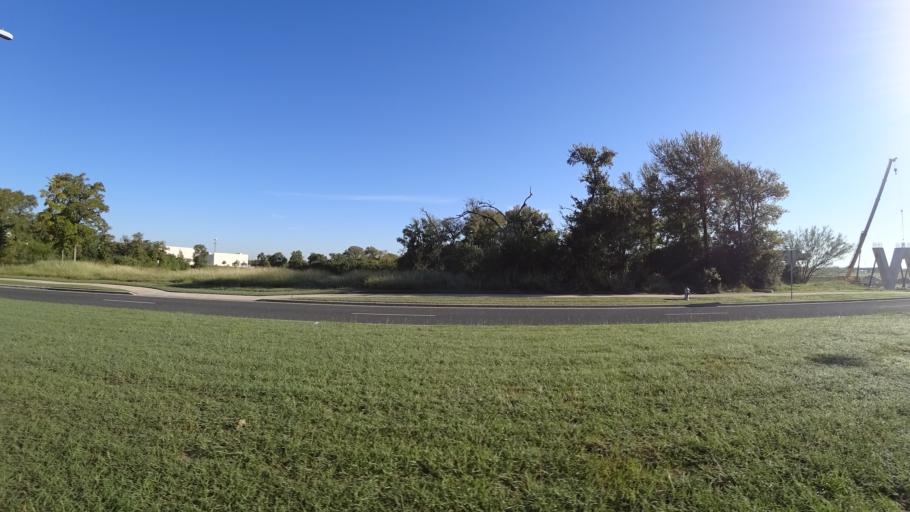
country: US
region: Texas
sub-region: Travis County
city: Austin
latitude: 30.2232
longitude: -97.6851
